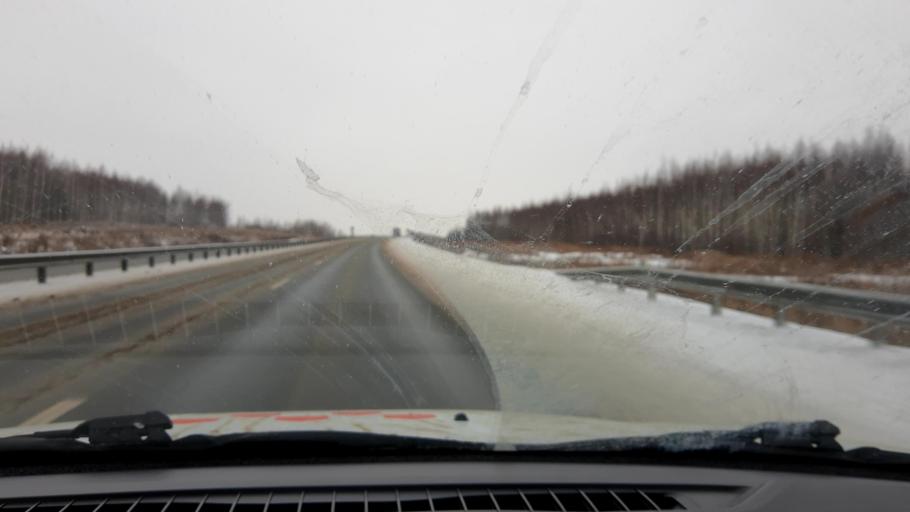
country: RU
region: Nizjnij Novgorod
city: Afonino
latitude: 56.1078
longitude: 43.9845
